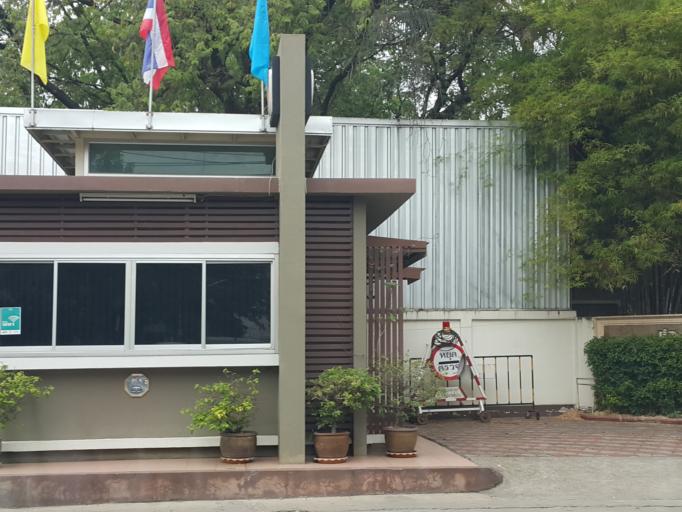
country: TH
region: Chiang Mai
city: Chiang Mai
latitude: 18.7978
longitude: 98.9792
